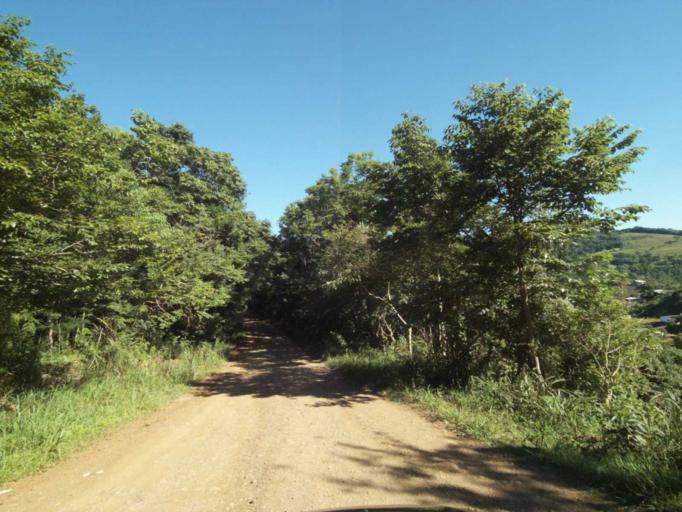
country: BR
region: Parana
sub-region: Francisco Beltrao
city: Francisco Beltrao
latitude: -26.1479
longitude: -53.3068
